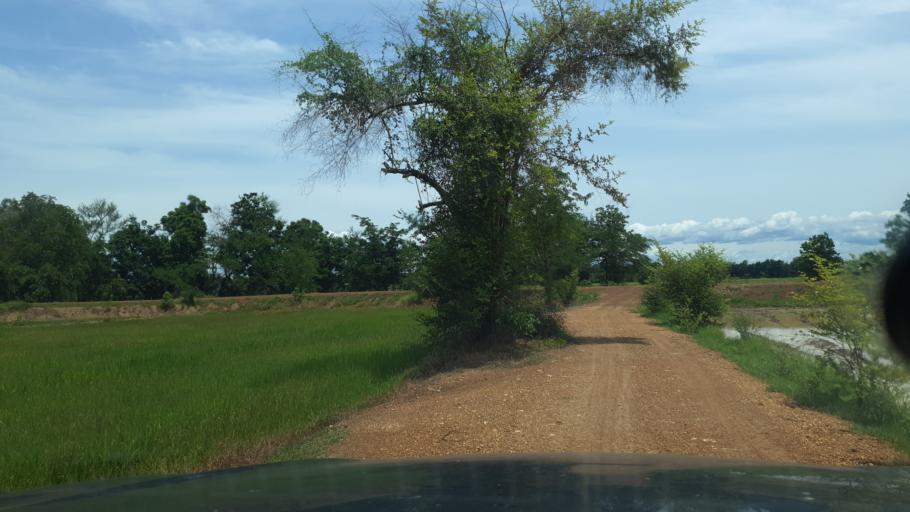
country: TH
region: Sukhothai
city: Ban Na
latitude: 17.0798
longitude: 99.6926
